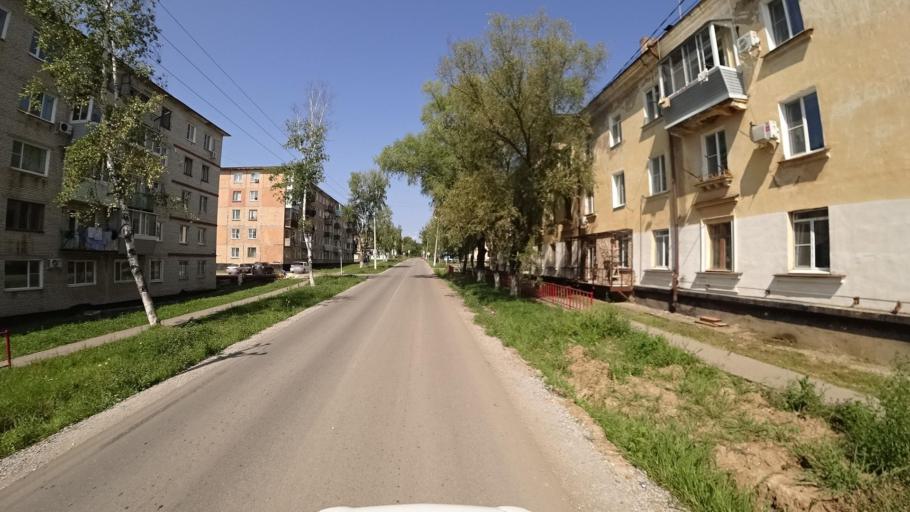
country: RU
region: Khabarovsk Krai
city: Khor
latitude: 47.9667
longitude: 135.1166
